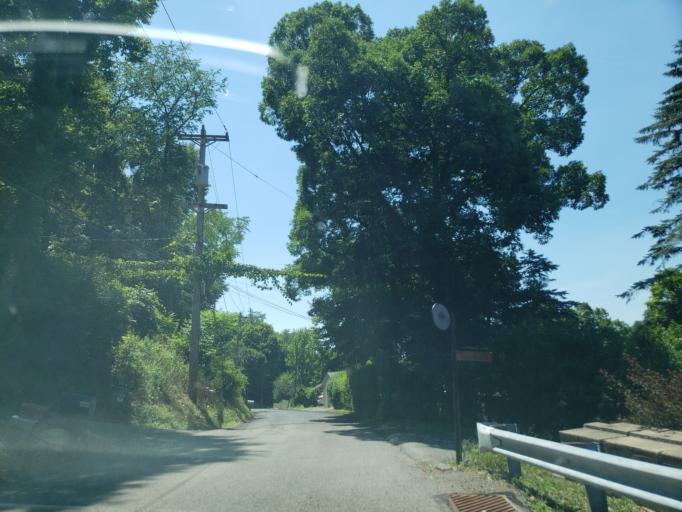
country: US
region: Pennsylvania
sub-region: Allegheny County
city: Emsworth
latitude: 40.5262
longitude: -80.0916
